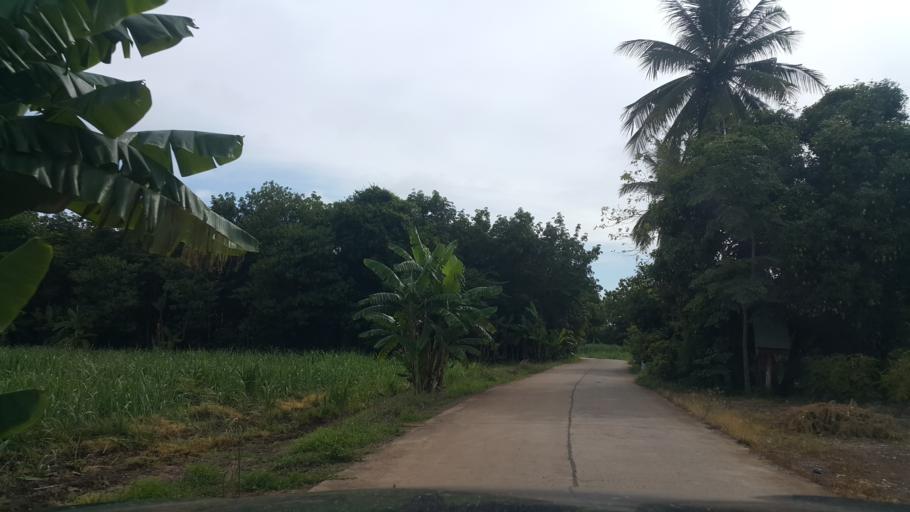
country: TH
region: Sukhothai
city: Sawankhalok
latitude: 17.2730
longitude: 99.8991
